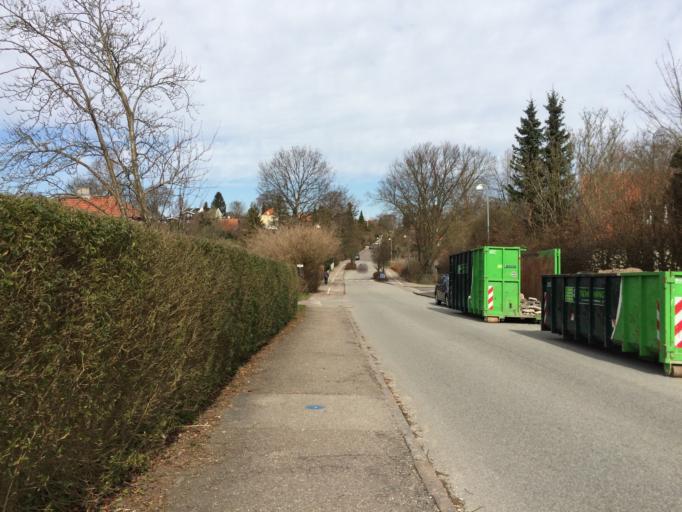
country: DK
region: Capital Region
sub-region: Horsholm Kommune
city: Horsholm
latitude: 55.8864
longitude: 12.5277
